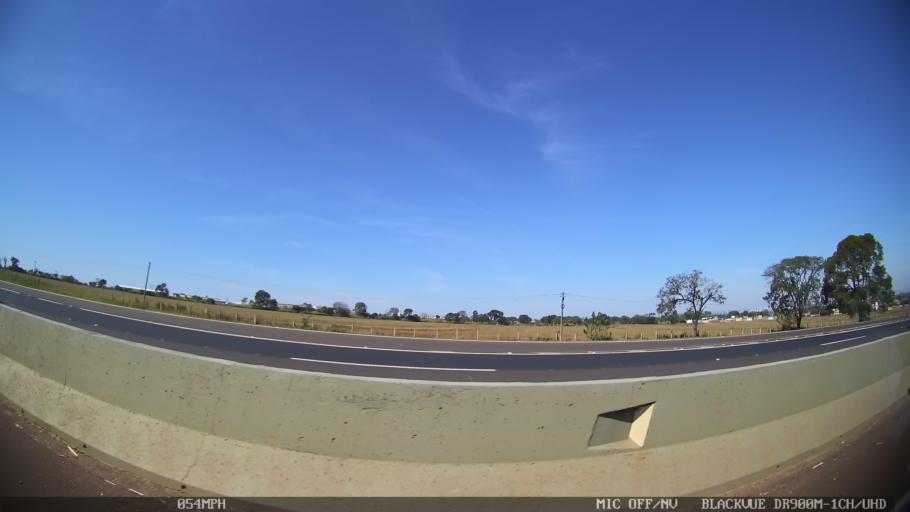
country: BR
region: Sao Paulo
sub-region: Ribeirao Preto
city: Ribeirao Preto
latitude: -21.0992
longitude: -47.7986
